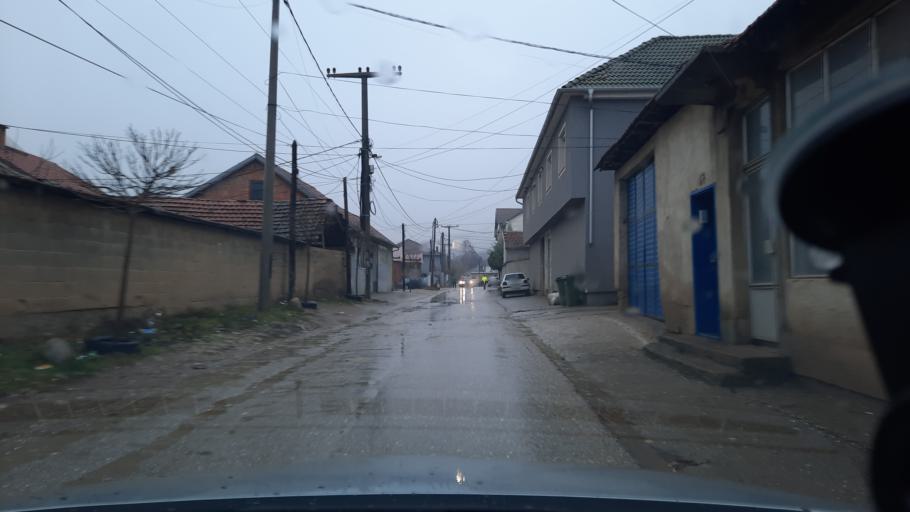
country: MK
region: Opstina Lipkovo
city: Lipkovo
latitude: 42.1557
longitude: 21.5856
